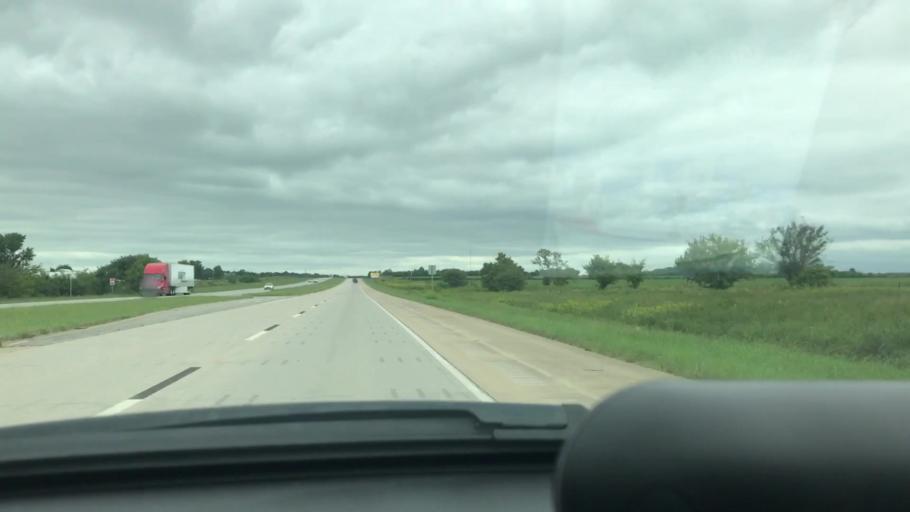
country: US
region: Oklahoma
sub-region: Mayes County
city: Chouteau
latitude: 36.0818
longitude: -95.3641
